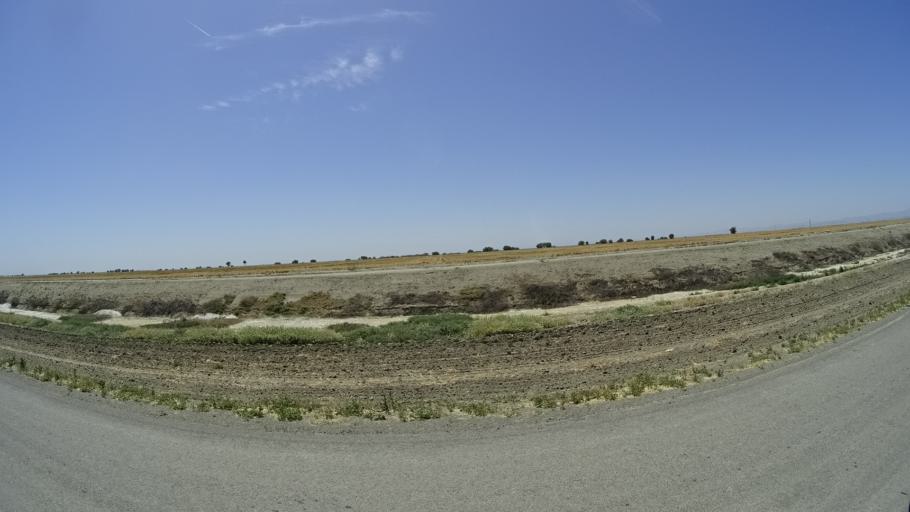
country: US
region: California
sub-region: Kings County
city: Stratford
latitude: 36.1525
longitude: -119.7356
